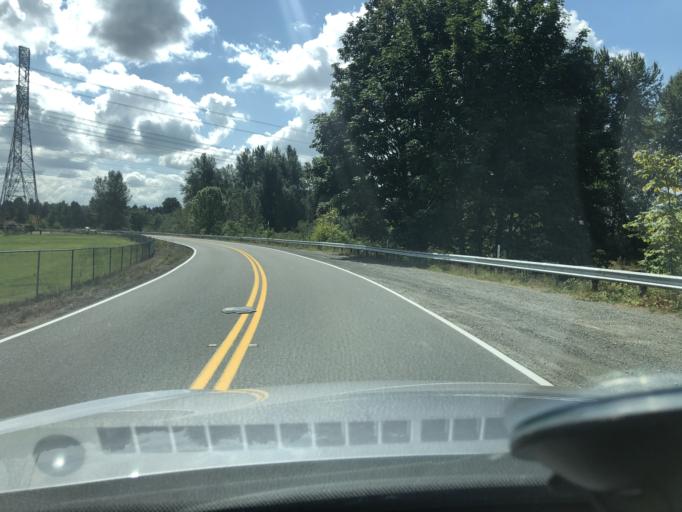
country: US
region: Washington
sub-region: King County
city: Lea Hill
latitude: 47.3390
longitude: -122.2083
